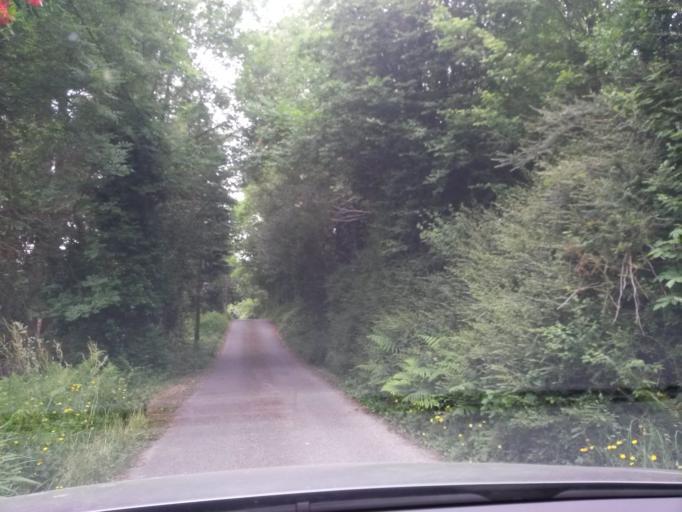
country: IE
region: Munster
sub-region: Ciarrai
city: Kenmare
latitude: 51.8566
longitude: -9.5176
